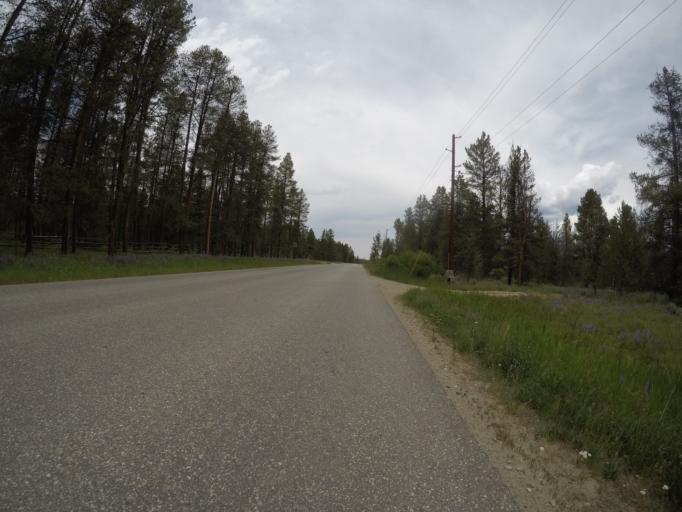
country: US
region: Colorado
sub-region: Grand County
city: Fraser
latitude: 39.9682
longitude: -105.8570
